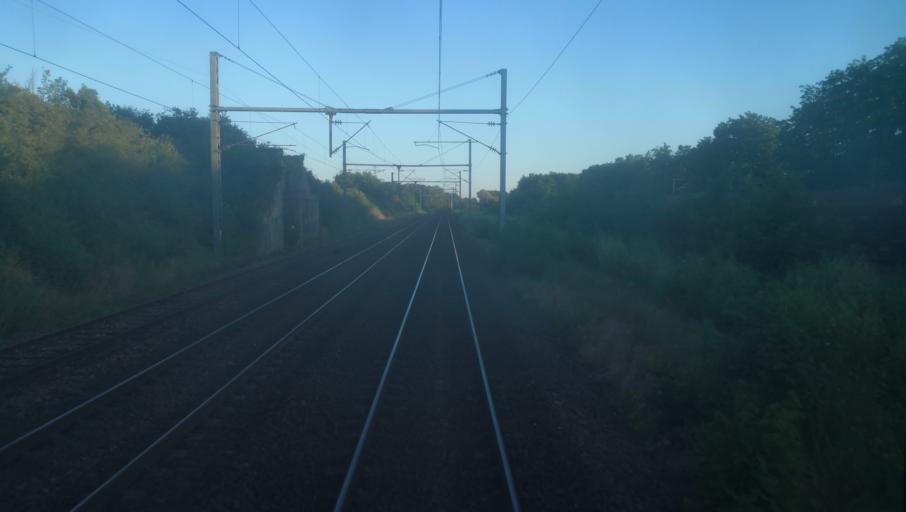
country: FR
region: Centre
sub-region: Departement du Cher
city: Cuffy
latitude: 46.9224
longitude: 3.0708
